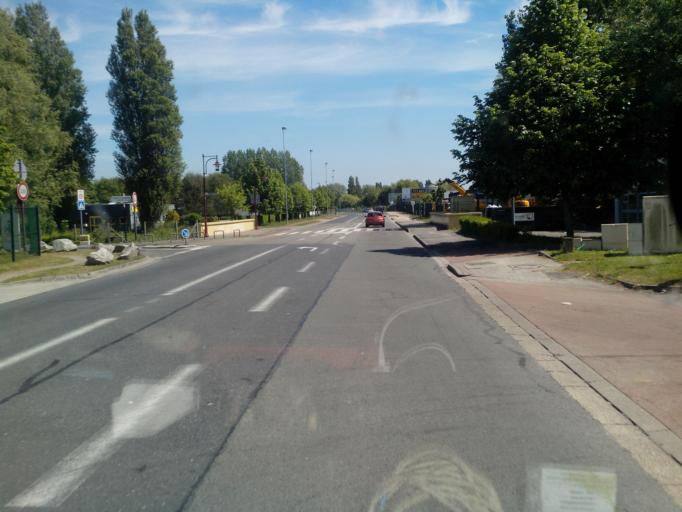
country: FR
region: Nord-Pas-de-Calais
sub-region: Departement du Pas-de-Calais
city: Saint-Leonard
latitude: 50.6890
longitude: 1.6191
